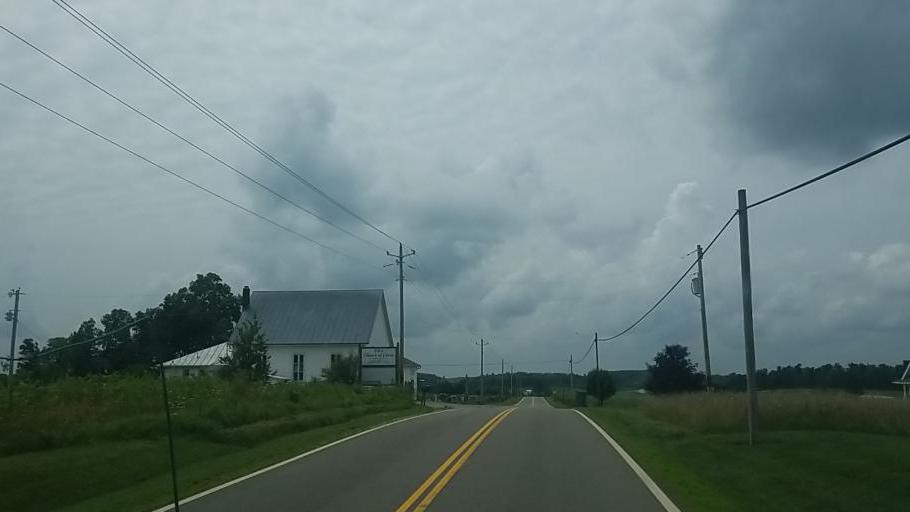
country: US
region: Ohio
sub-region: Licking County
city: Utica
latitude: 40.2018
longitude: -82.3551
